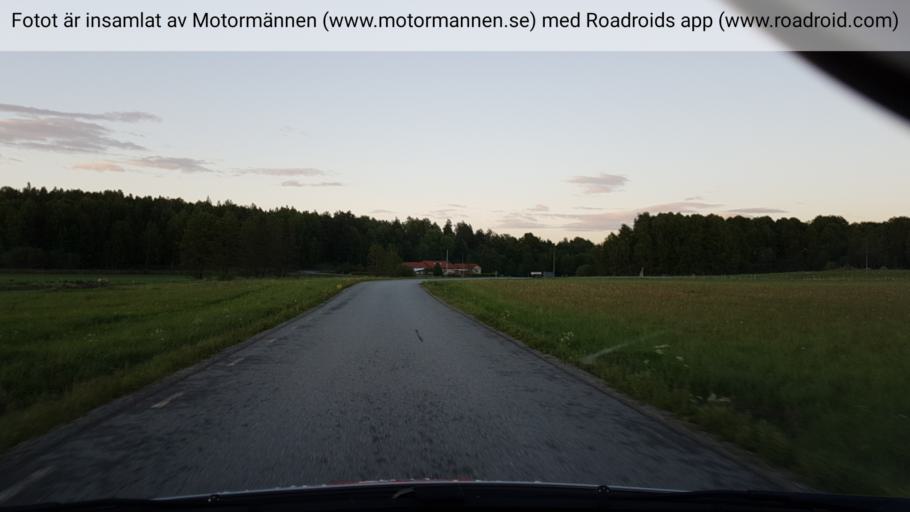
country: SE
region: Vaestmanland
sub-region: Vasteras
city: Hokasen
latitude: 59.7020
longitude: 16.5170
